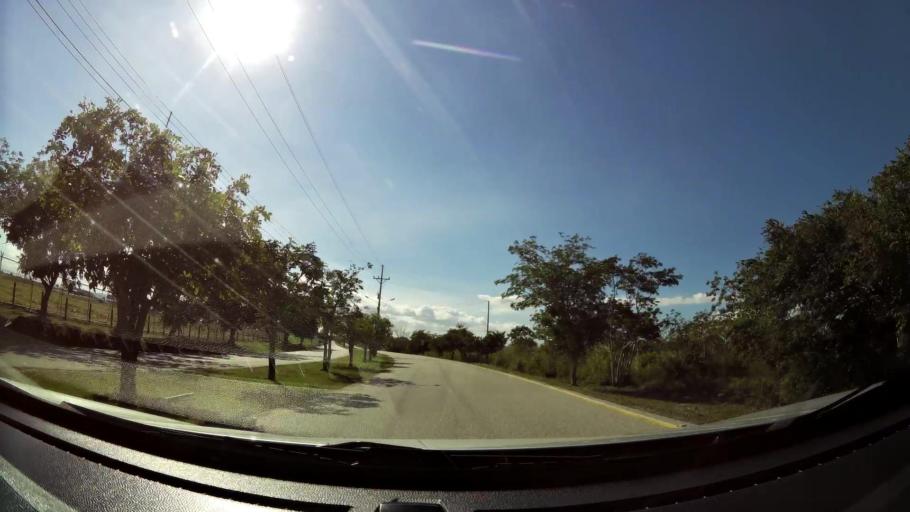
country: CR
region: Guanacaste
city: Liberia
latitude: 10.6028
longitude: -85.5326
